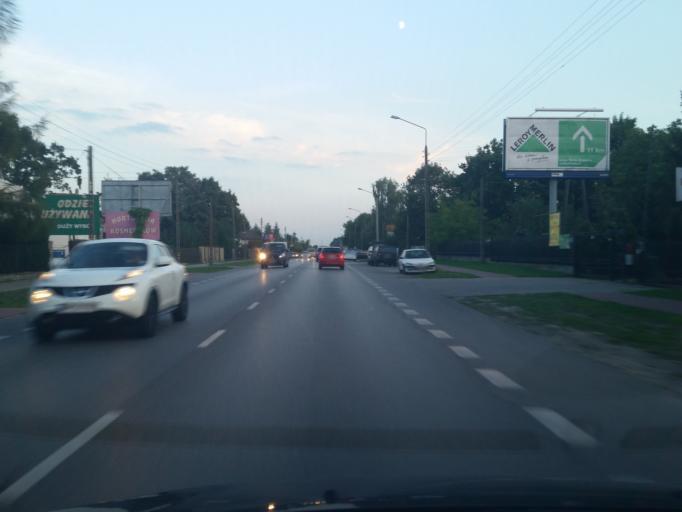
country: PL
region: Masovian Voivodeship
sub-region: Powiat legionowski
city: Jablonna
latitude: 52.3734
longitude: 20.9263
